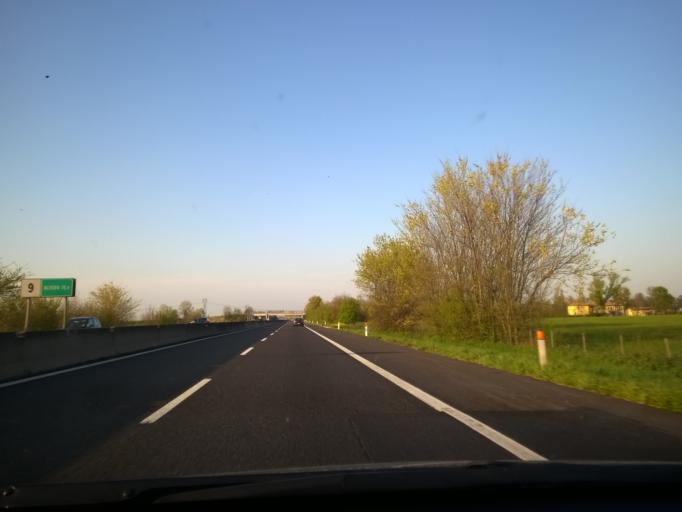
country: IT
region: Emilia-Romagna
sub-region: Provincia di Bologna
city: Bentivoglio
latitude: 44.6003
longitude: 11.4061
